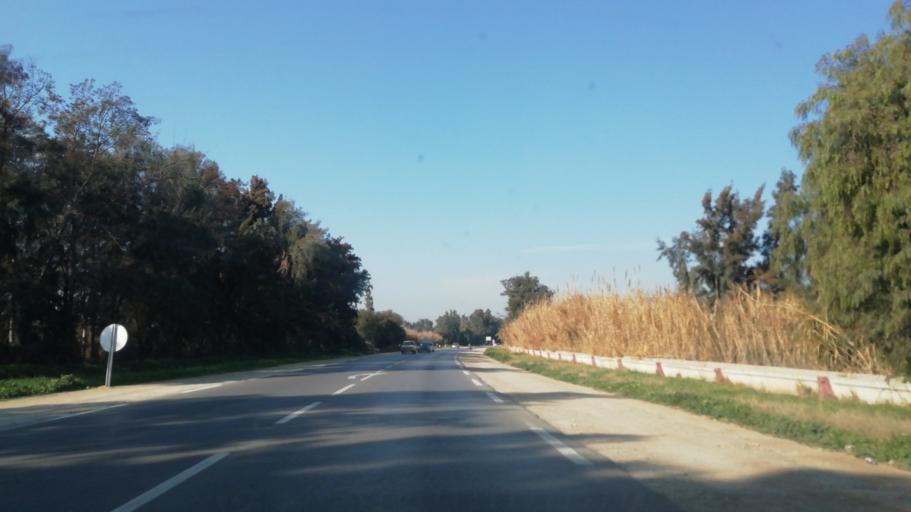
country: DZ
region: Relizane
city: Relizane
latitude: 35.7232
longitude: 0.4869
